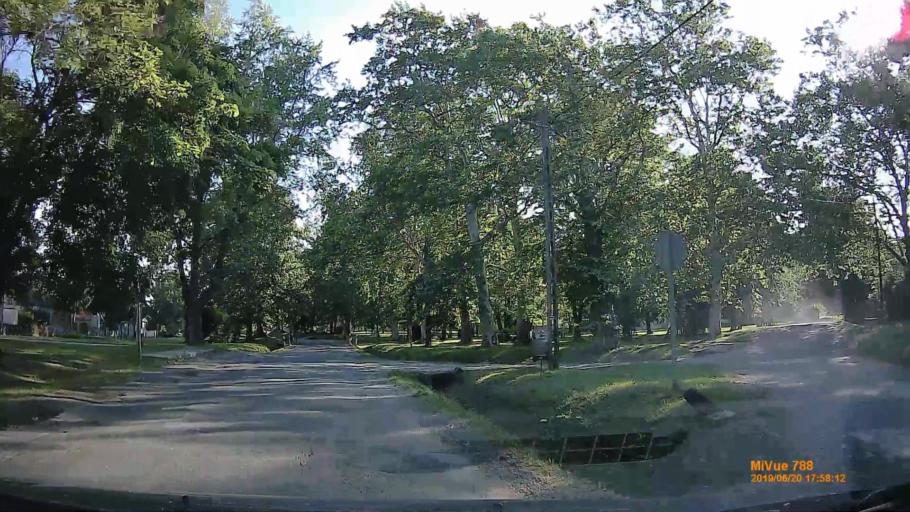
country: HU
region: Baranya
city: Buekkoesd
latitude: 46.1060
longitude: 17.9921
